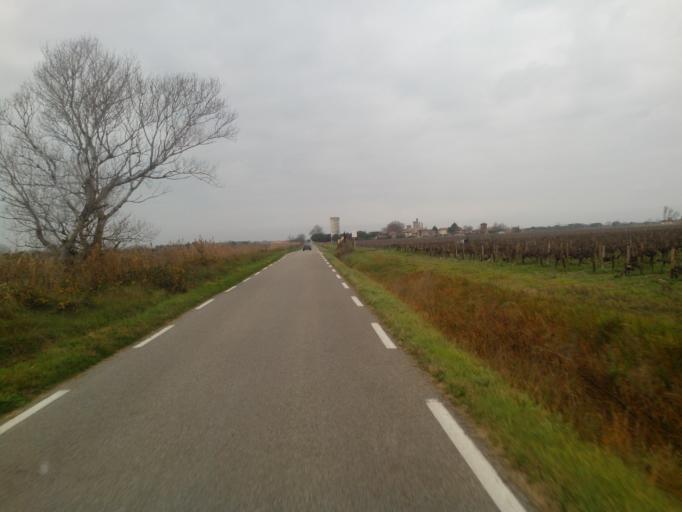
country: FR
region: Languedoc-Roussillon
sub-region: Departement du Gard
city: Aigues-Mortes
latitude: 43.5687
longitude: 4.3225
